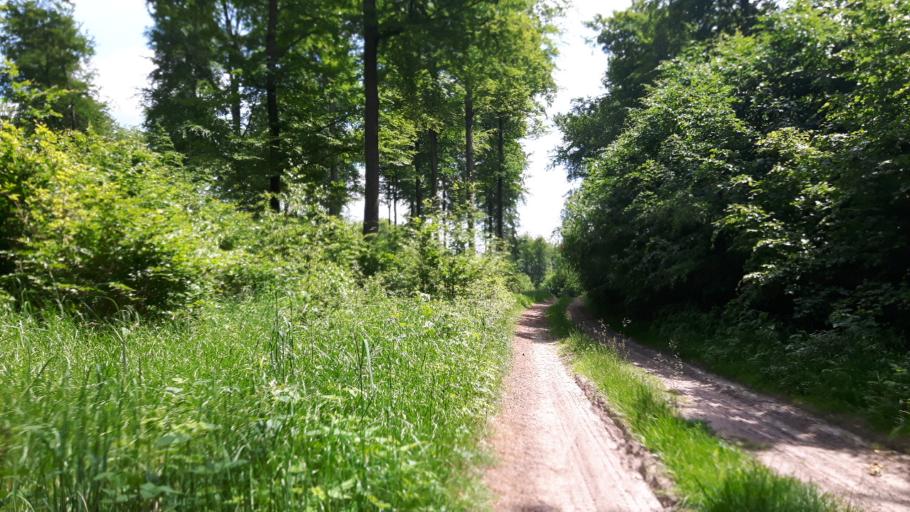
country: PL
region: West Pomeranian Voivodeship
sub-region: Powiat goleniowski
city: Osina
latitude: 53.6488
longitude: 14.9183
